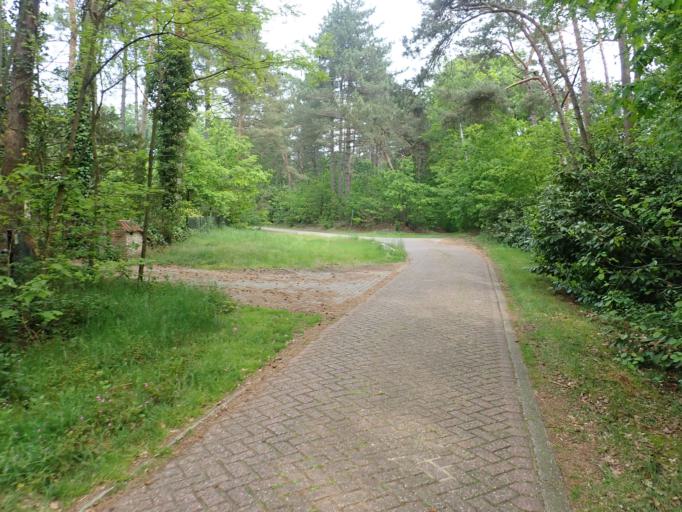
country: BE
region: Flanders
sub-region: Provincie Antwerpen
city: Oud-Turnhout
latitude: 51.2981
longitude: 5.0066
